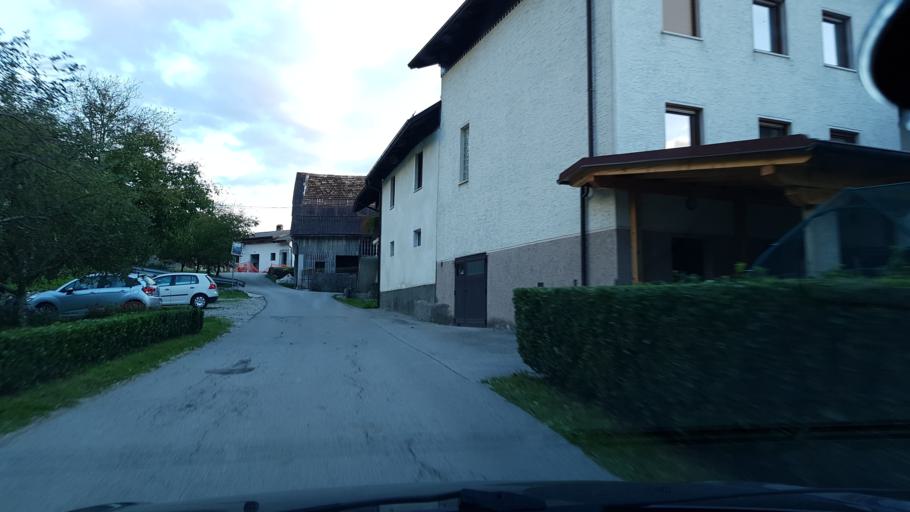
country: SI
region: Kobarid
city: Kobarid
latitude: 46.2584
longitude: 13.6142
